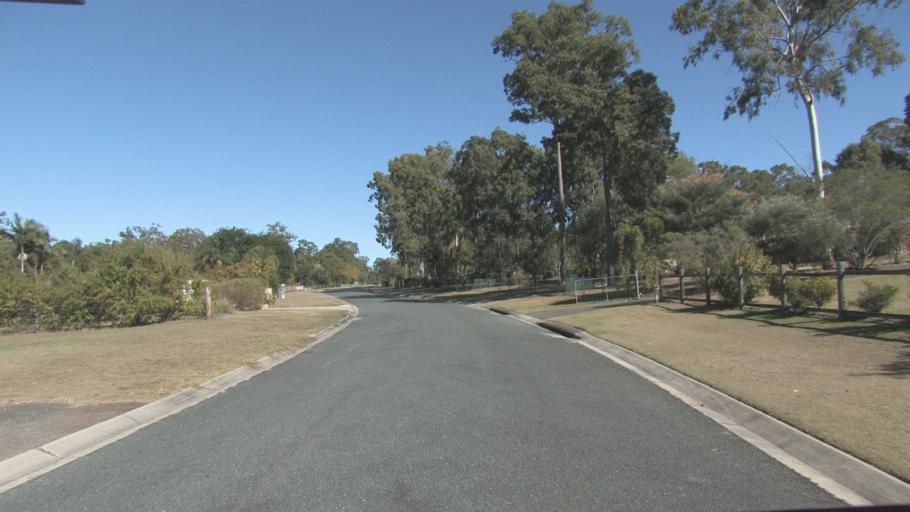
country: AU
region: Queensland
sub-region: Logan
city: North Maclean
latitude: -27.8191
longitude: 152.9483
